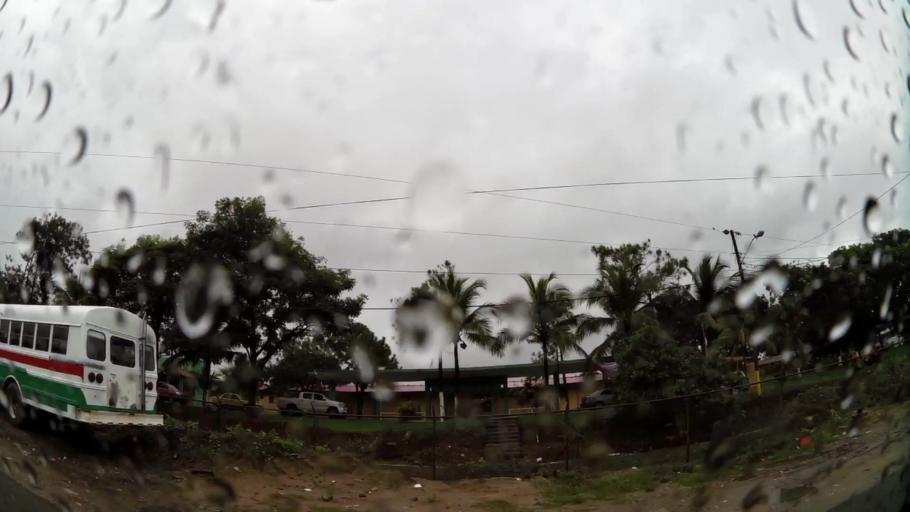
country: PA
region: Colon
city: Arco Iris
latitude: 9.3348
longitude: -79.8776
